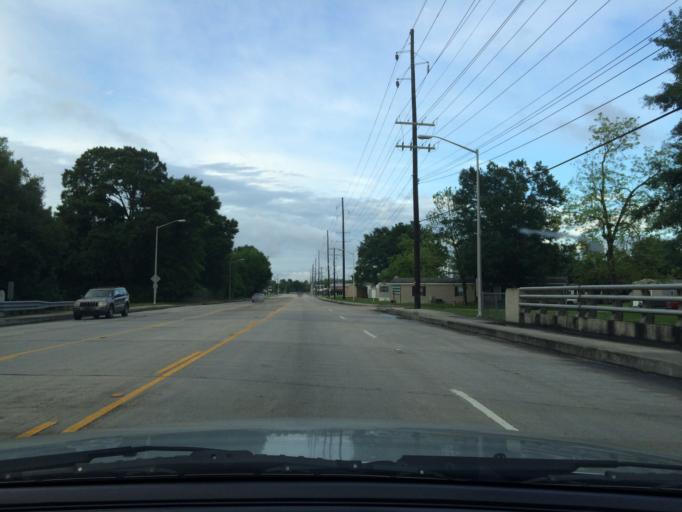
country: US
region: Louisiana
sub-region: Lafayette Parish
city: Scott
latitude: 30.2197
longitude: -92.0643
